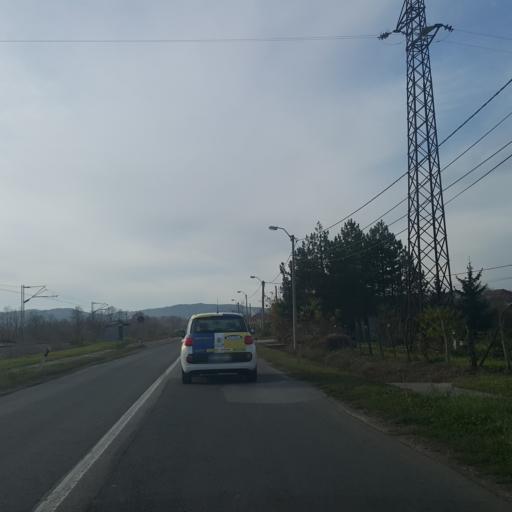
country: RS
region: Central Serbia
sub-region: Kolubarski Okrug
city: Lajkovac
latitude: 44.3647
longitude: 20.1397
